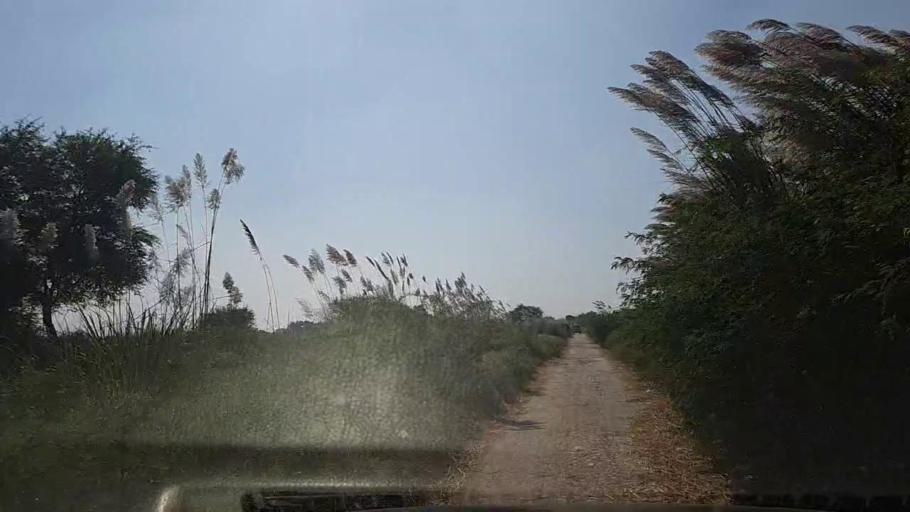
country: PK
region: Sindh
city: Daro Mehar
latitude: 24.8192
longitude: 68.0828
